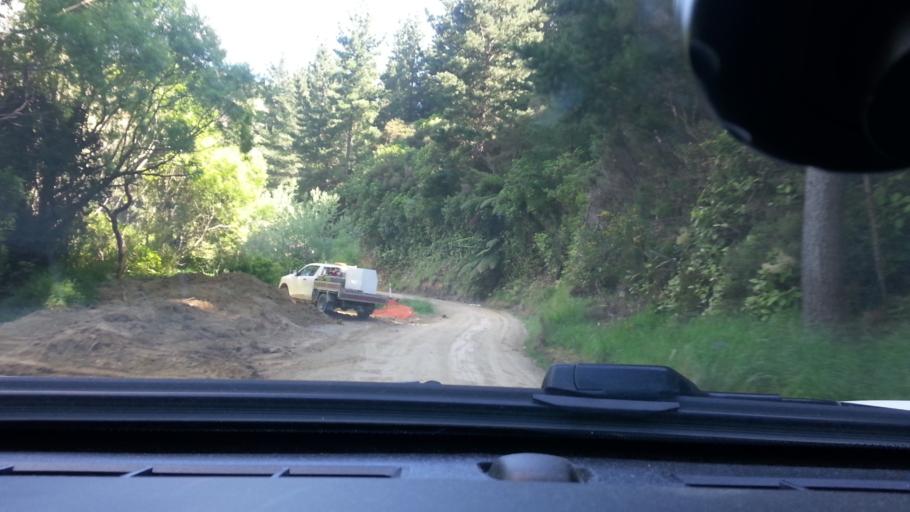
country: NZ
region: Wellington
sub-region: South Wairarapa District
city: Waipawa
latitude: -41.3563
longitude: 175.3986
